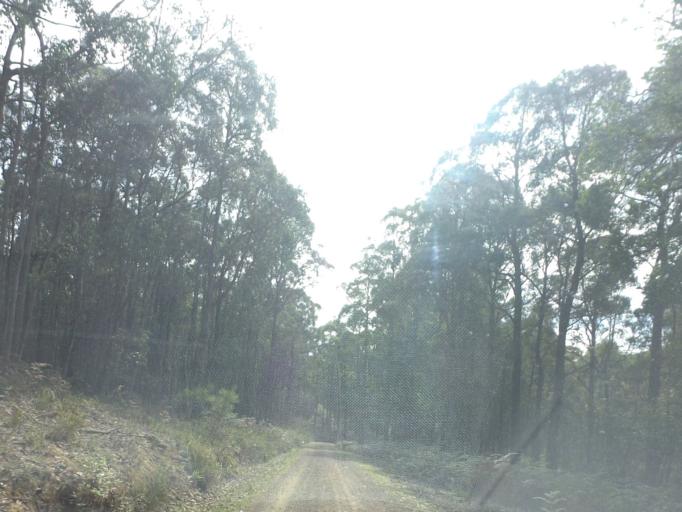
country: AU
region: Victoria
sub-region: Moorabool
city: Bacchus Marsh
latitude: -37.4377
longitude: 144.2676
